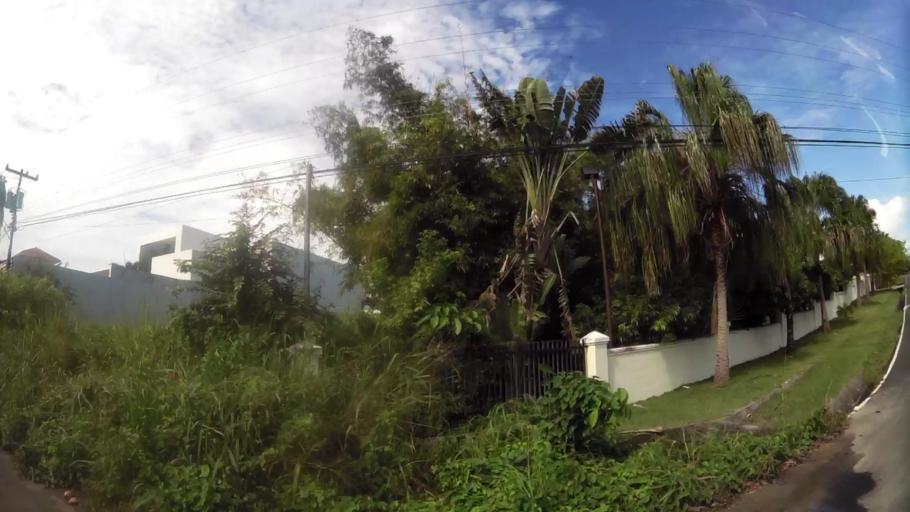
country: PA
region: Panama
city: Nueva Gorgona
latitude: 8.5460
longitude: -79.8779
